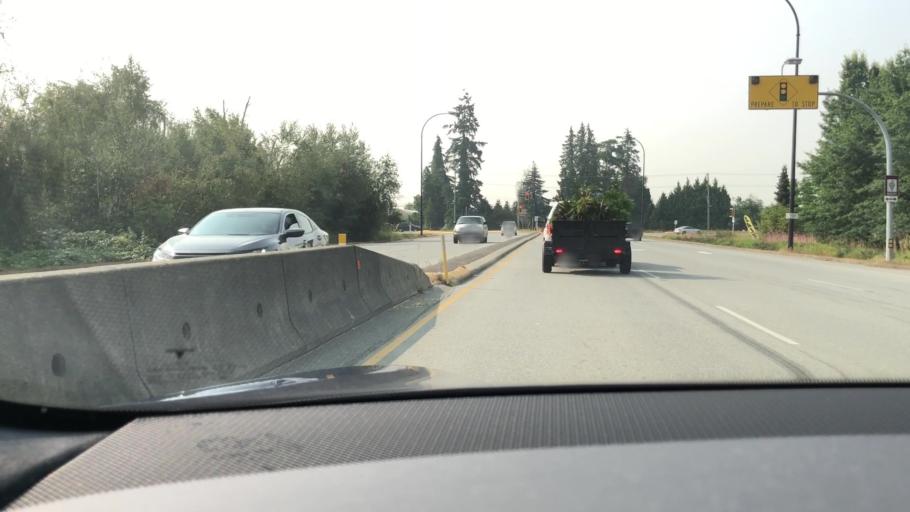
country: CA
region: British Columbia
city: Richmond
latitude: 49.1715
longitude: -123.0745
